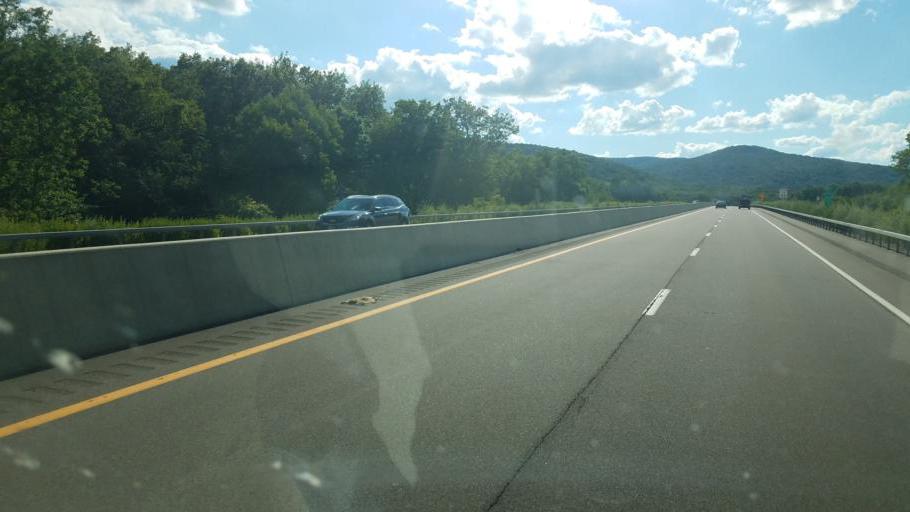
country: US
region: New York
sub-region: Cattaraugus County
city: Salamanca
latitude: 42.0900
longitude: -78.6401
